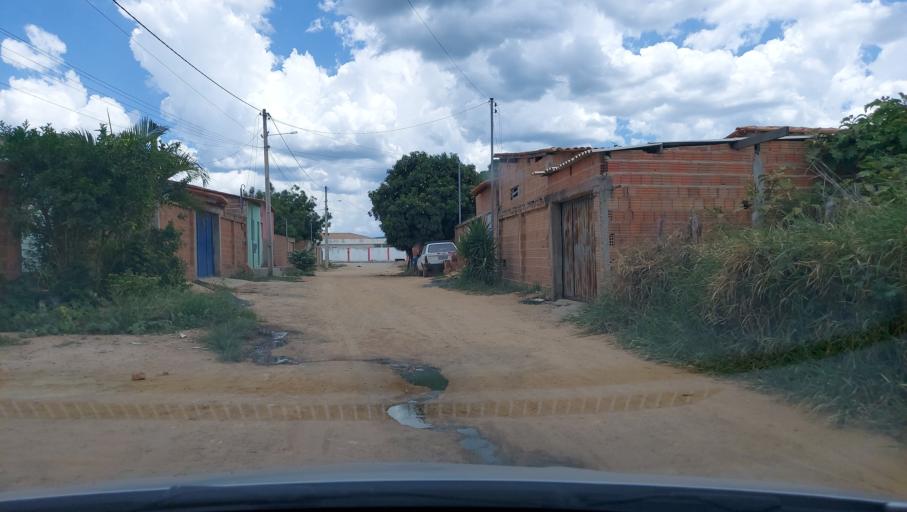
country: BR
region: Bahia
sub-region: Oliveira Dos Brejinhos
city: Beira Rio
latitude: -12.0050
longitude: -42.6303
